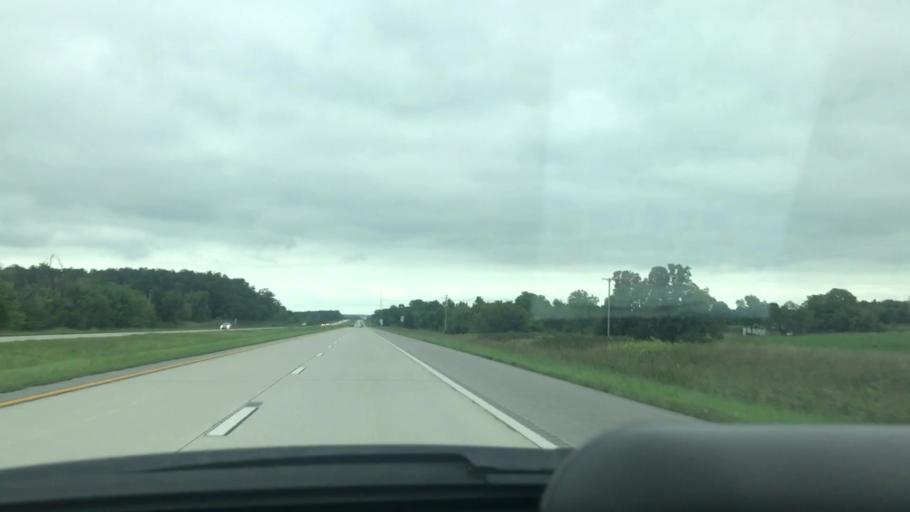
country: US
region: Missouri
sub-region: Greene County
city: Fair Grove
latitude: 37.4867
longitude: -93.1391
